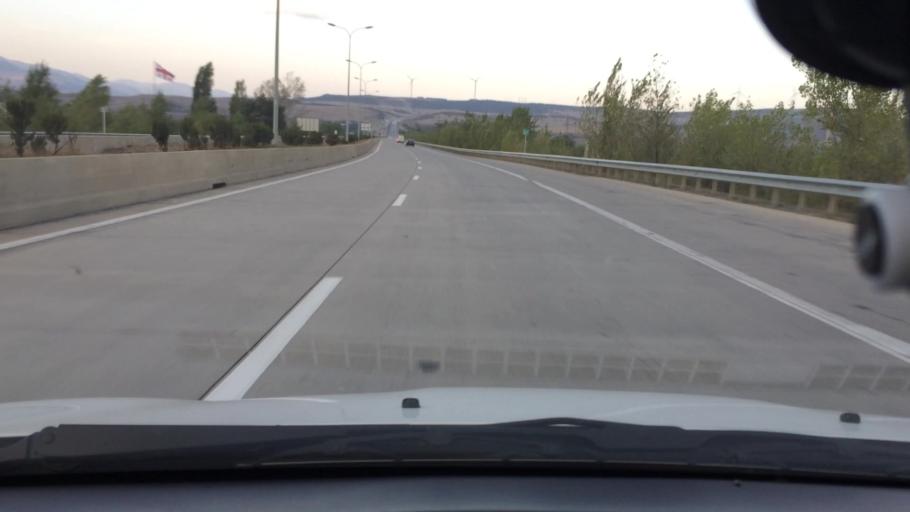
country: GE
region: Shida Kartli
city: Gori
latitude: 42.0184
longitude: 44.1026
